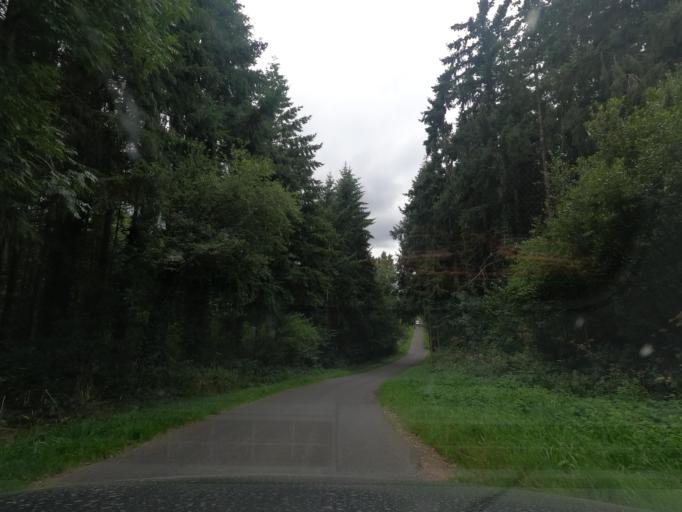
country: FR
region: Lower Normandy
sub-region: Departement de l'Orne
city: Briouze
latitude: 48.7196
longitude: -0.3253
